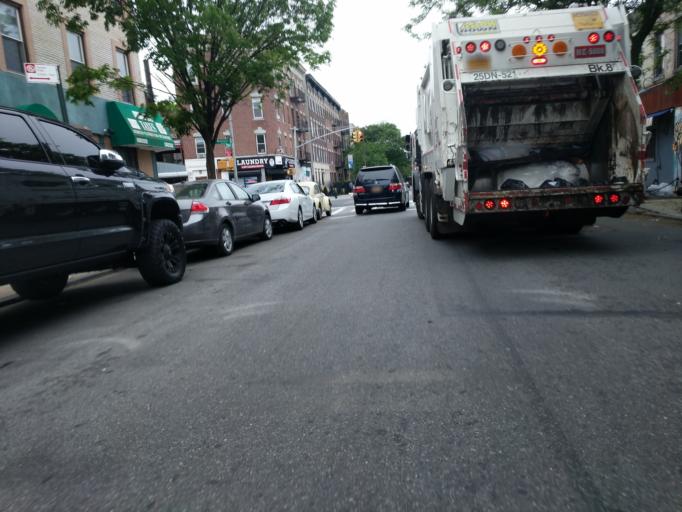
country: US
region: New York
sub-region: Kings County
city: Brooklyn
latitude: 40.6765
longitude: -73.9630
